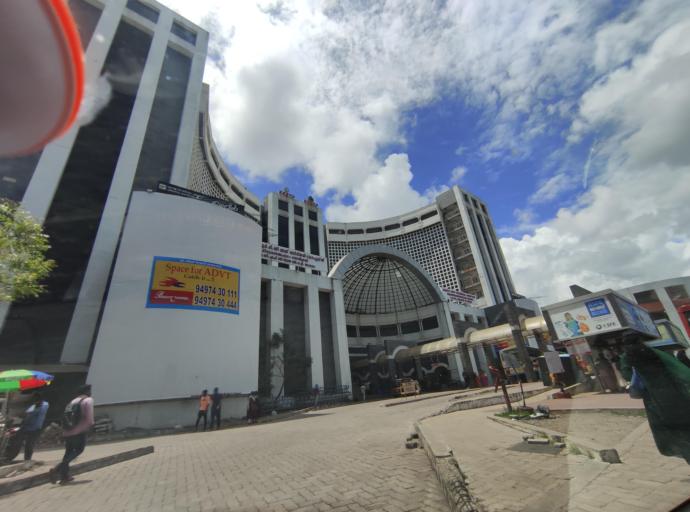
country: IN
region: Kerala
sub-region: Thiruvananthapuram
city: Thiruvananthapuram
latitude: 8.4879
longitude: 76.9521
